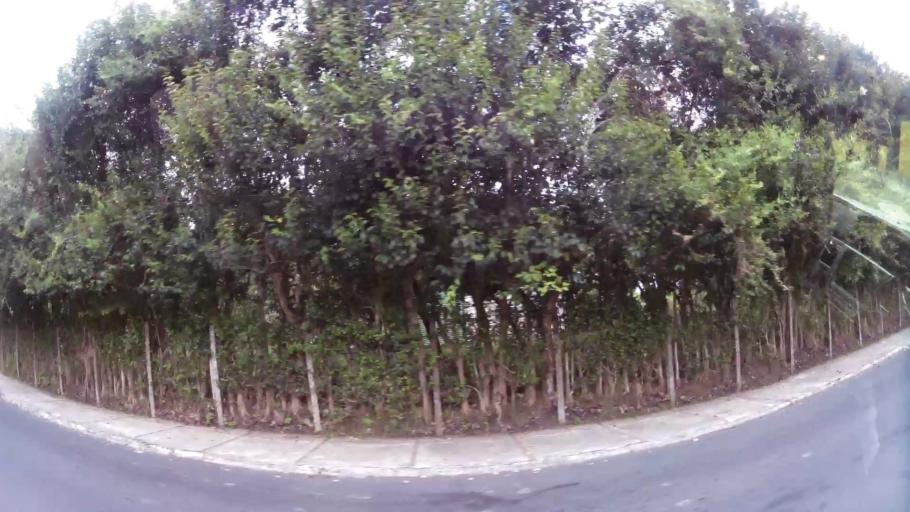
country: GT
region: Guatemala
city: Guatemala City
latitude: 14.6298
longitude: -90.5474
